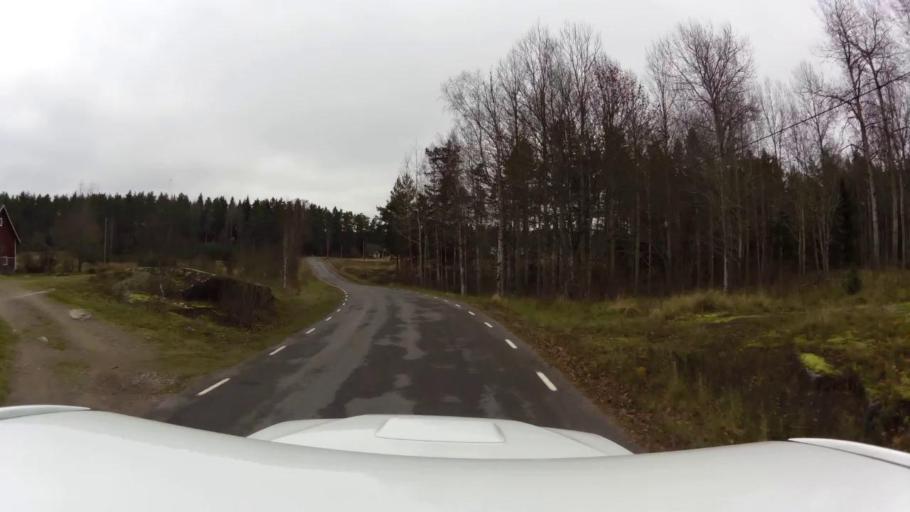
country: SE
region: OEstergoetland
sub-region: Kinda Kommun
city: Kisa
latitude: 58.1323
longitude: 15.4536
